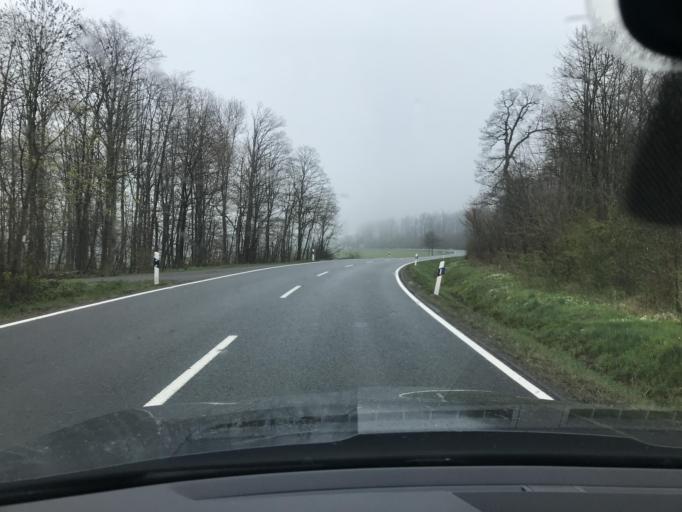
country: DE
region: Saxony-Anhalt
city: Harzgerode
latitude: 51.6211
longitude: 11.1560
